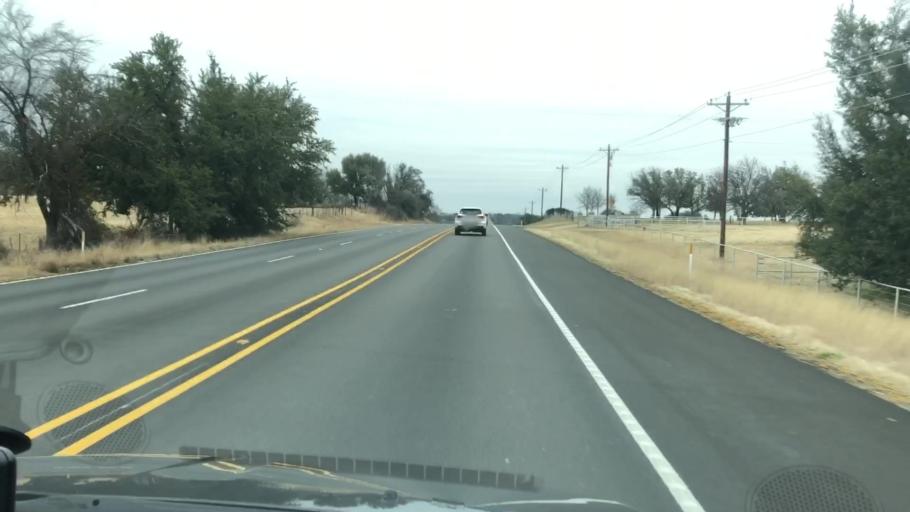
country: US
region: Texas
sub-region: Erath County
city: Stephenville
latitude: 32.3081
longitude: -98.1853
